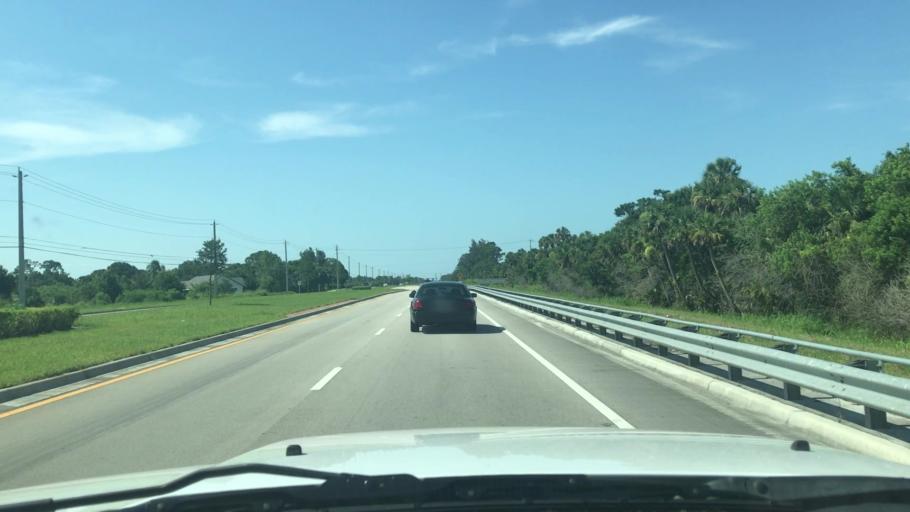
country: US
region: Florida
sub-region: Indian River County
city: West Vero Corridor
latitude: 27.6581
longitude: -80.4630
